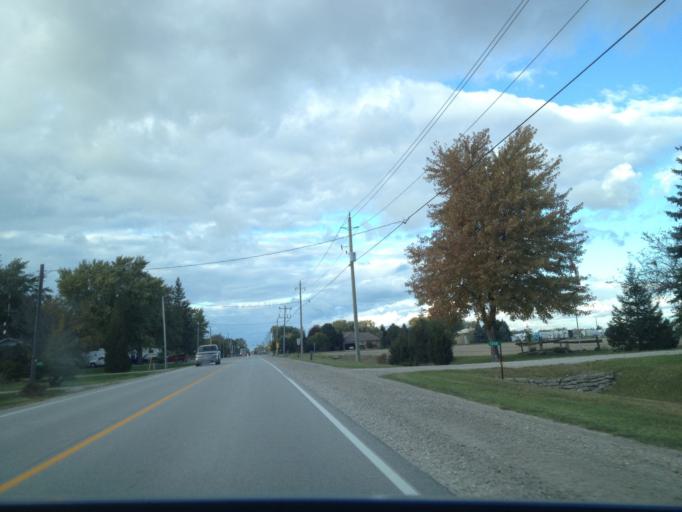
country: US
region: Michigan
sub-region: Wayne County
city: Grosse Pointe Farms
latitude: 42.2704
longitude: -82.7133
